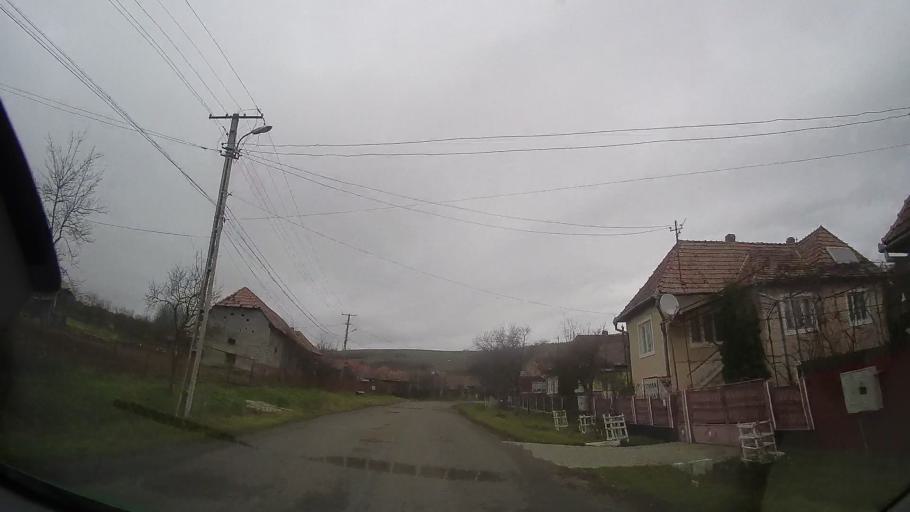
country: RO
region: Mures
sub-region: Comuna Bala
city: Bala
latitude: 46.7126
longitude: 24.5013
